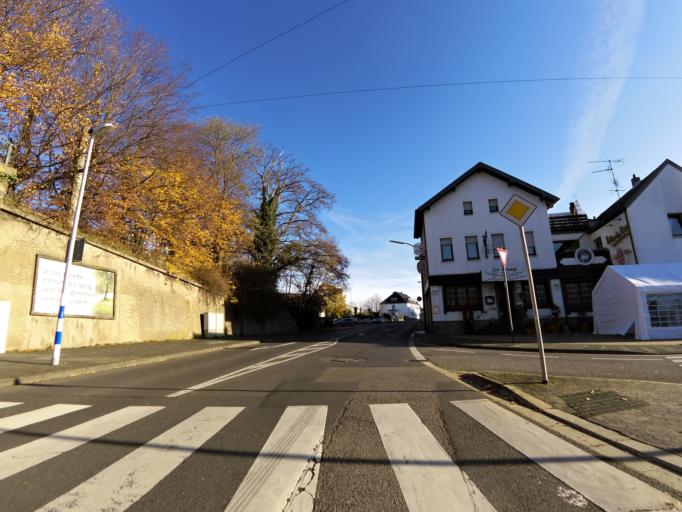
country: DE
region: North Rhine-Westphalia
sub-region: Regierungsbezirk Koln
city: Euskirchen
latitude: 50.6567
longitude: 6.7877
